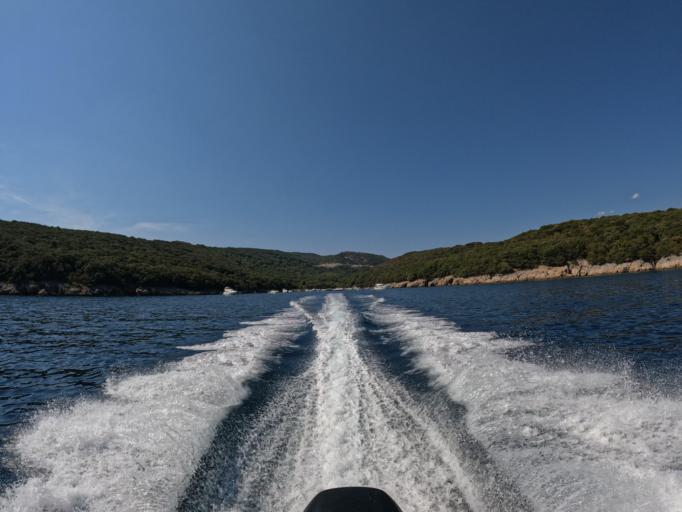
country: HR
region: Primorsko-Goranska
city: Cres
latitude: 44.9489
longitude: 14.4648
